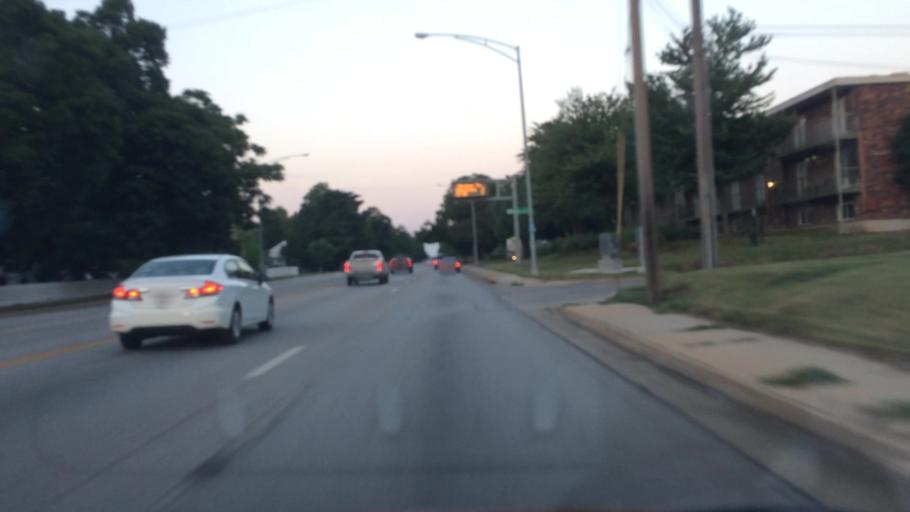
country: US
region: Missouri
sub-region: Greene County
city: Springfield
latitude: 37.1820
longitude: -93.2860
